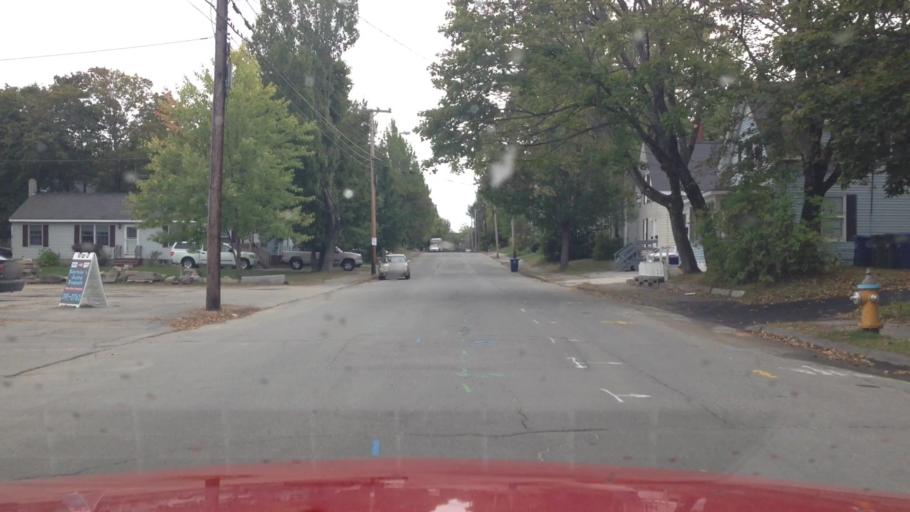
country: US
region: Maine
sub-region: Cumberland County
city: Westbrook
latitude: 43.6787
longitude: -70.3511
